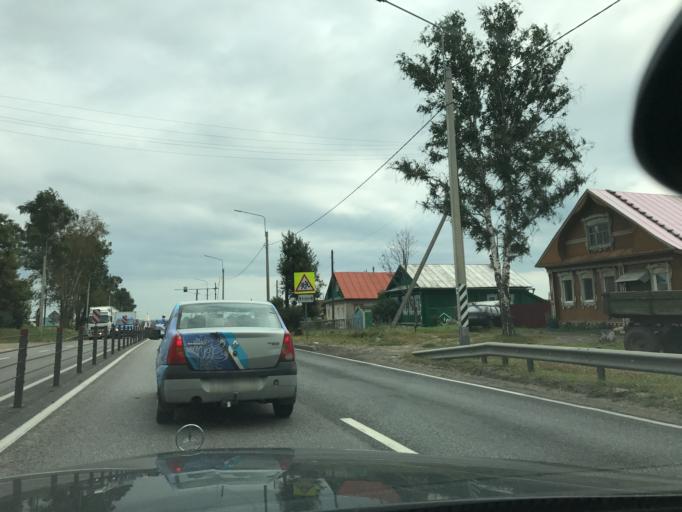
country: RU
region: Vladimir
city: Gorokhovets
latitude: 56.1927
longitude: 42.6883
